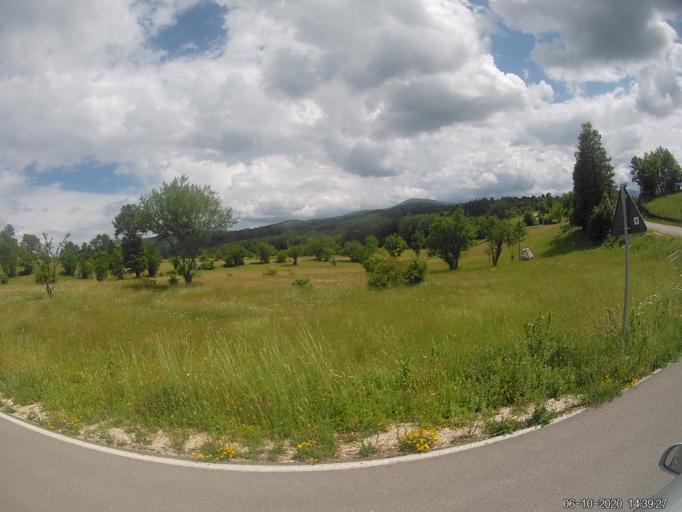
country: XK
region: Prizren
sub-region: Komuna e Therandes
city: Budakovo
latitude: 42.4004
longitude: 20.9456
